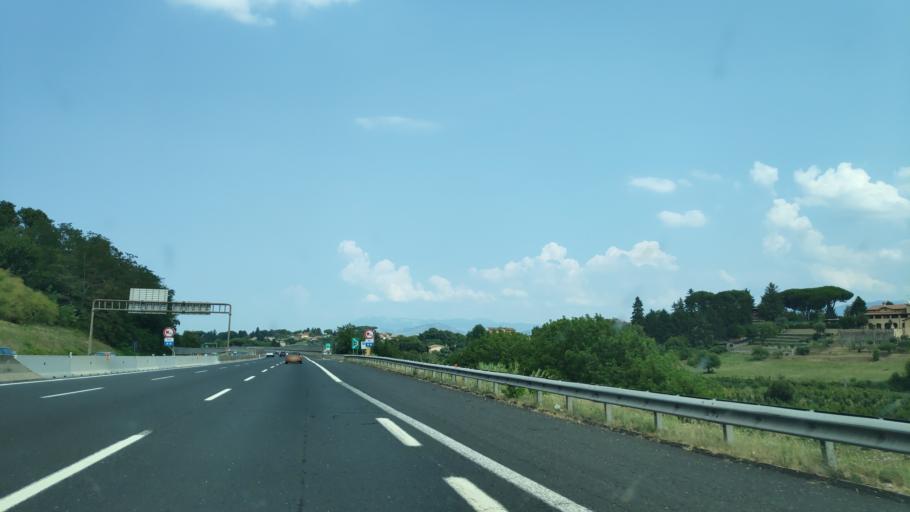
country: IT
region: Latium
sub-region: Citta metropolitana di Roma Capitale
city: San Cesareo
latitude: 41.8154
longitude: 12.8081
